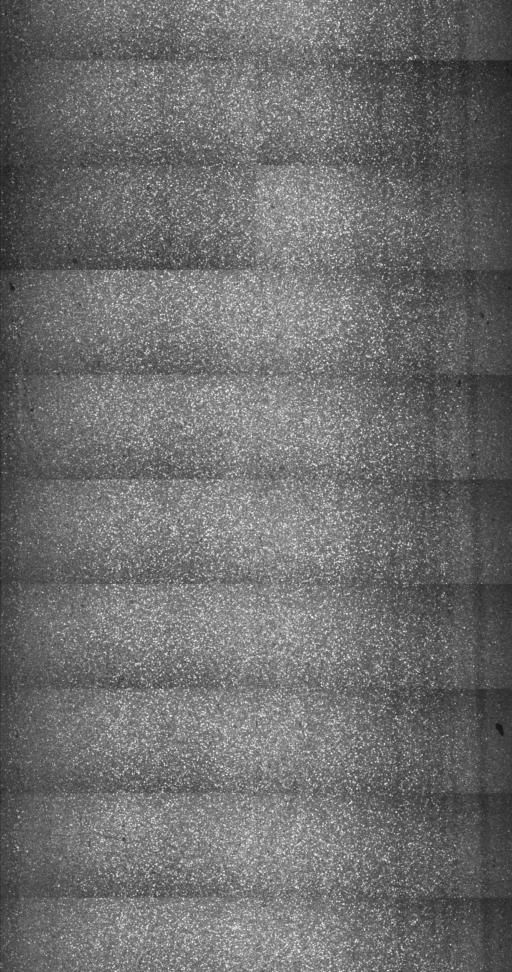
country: US
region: Vermont
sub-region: Chittenden County
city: Essex Junction
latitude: 44.4754
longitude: -73.1133
